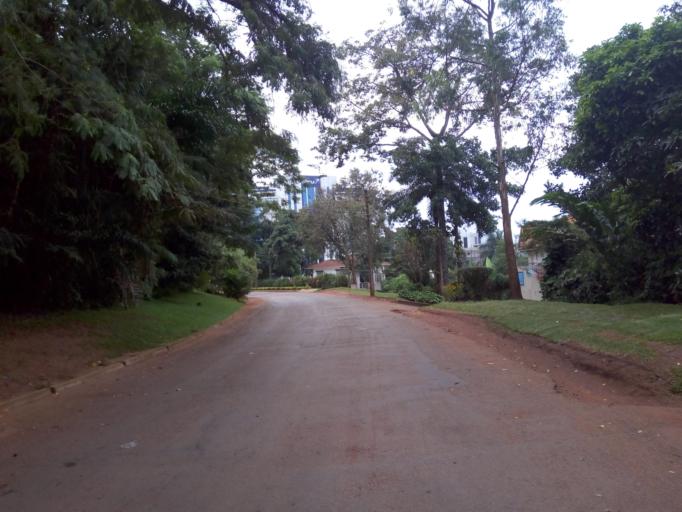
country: UG
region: Central Region
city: Kampala Central Division
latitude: 0.3247
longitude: 32.5826
